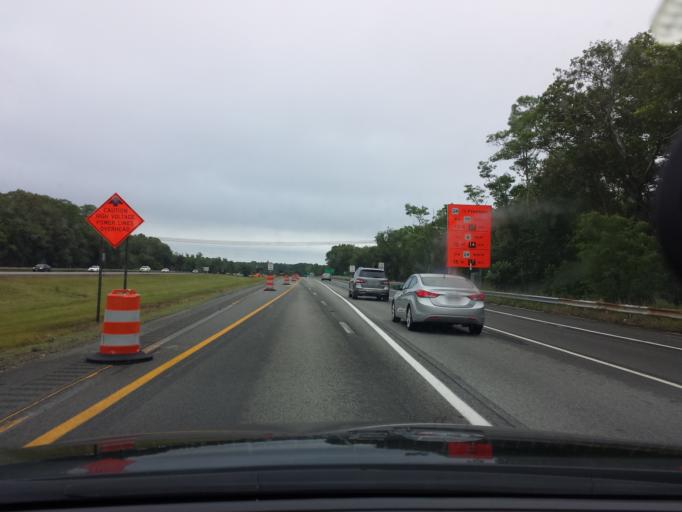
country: US
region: Massachusetts
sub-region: Bristol County
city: Ocean Grove
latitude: 41.7426
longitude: -71.2109
